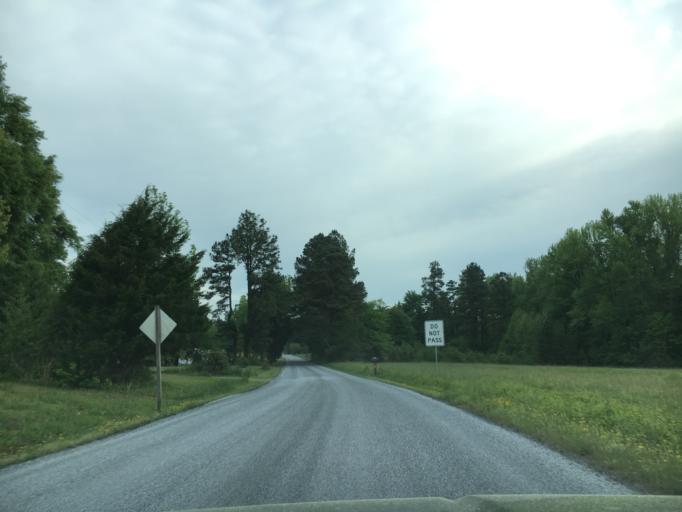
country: US
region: Virginia
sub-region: Campbell County
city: Brookneal
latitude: 36.9244
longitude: -78.9496
